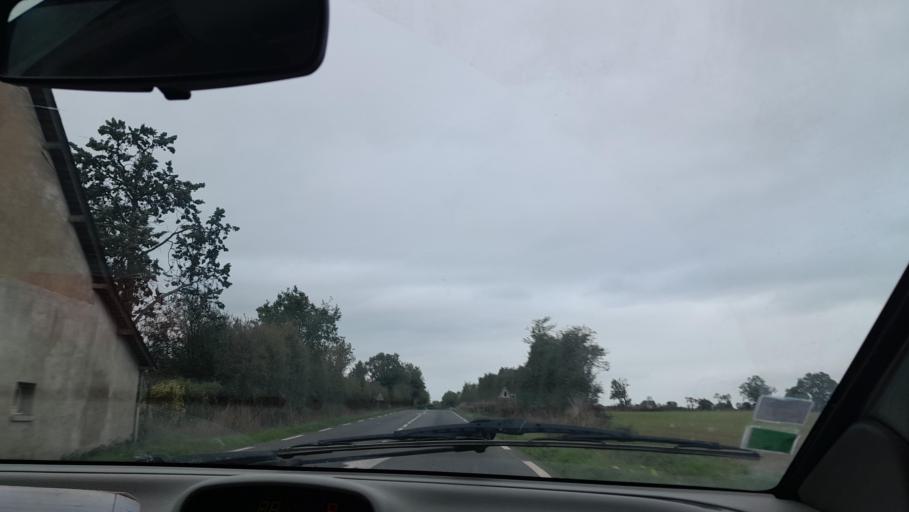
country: FR
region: Pays de la Loire
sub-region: Departement de Maine-et-Loire
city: Pouance
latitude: 47.6482
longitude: -1.2006
